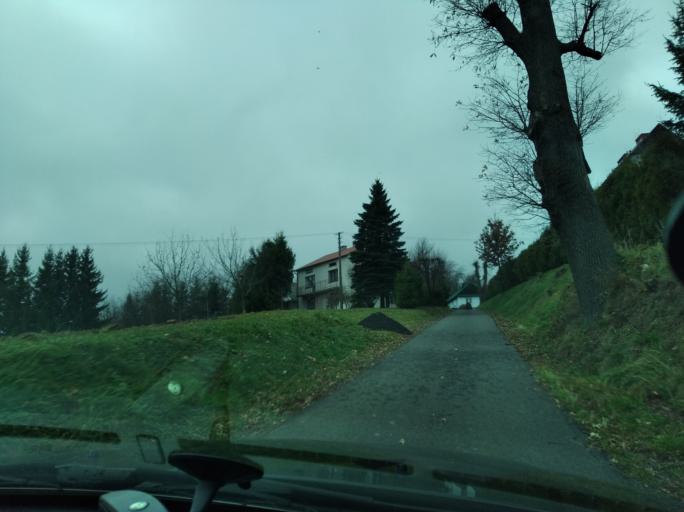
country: PL
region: Subcarpathian Voivodeship
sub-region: Powiat przeworski
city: Jawornik Polski
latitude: 49.8891
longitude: 22.2787
